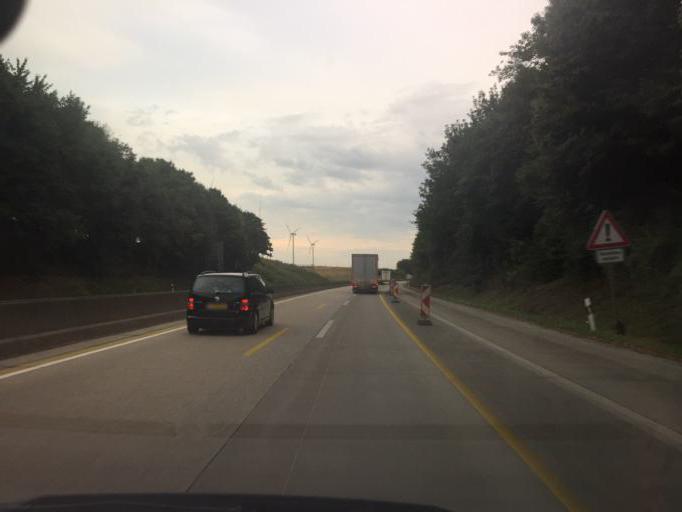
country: DE
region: North Rhine-Westphalia
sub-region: Regierungsbezirk Koln
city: Titz
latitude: 51.0298
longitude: 6.4781
